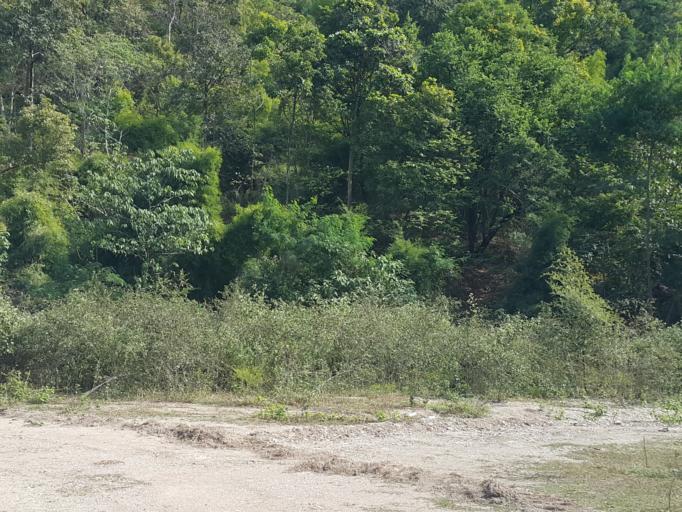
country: TH
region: Lampang
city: Mae Mo
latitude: 18.3267
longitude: 99.7641
